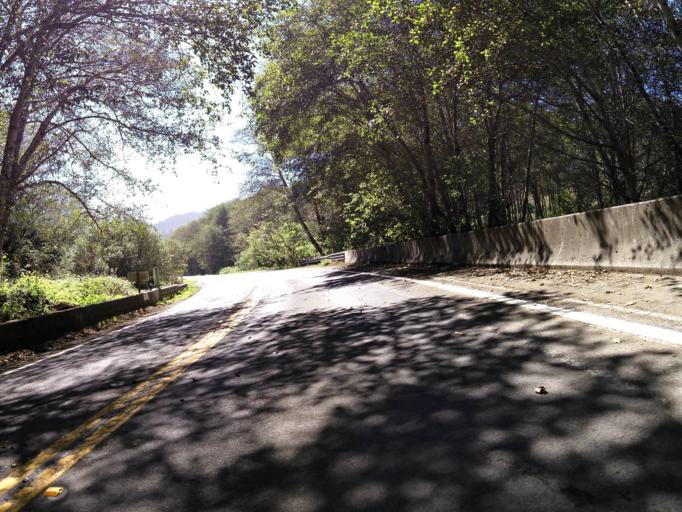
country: US
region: California
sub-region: Mendocino County
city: Fort Bragg
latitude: 39.7770
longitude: -123.8329
